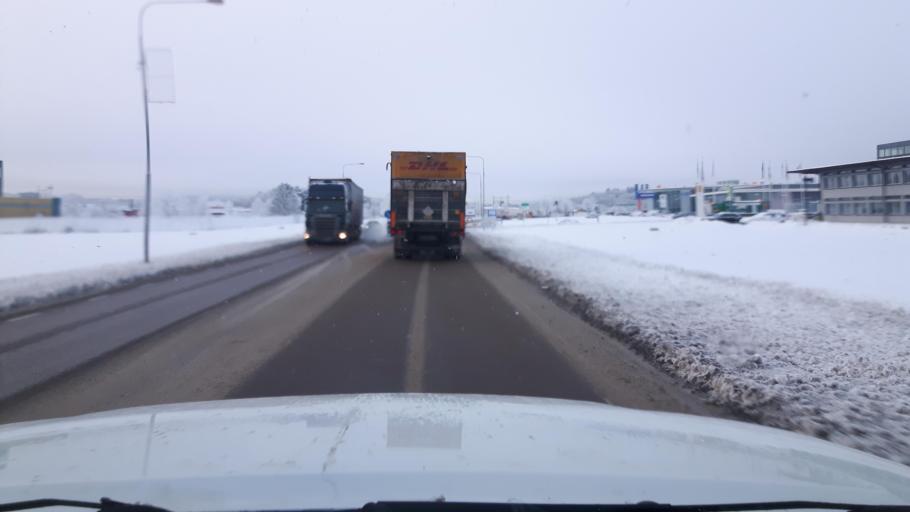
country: SE
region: Halland
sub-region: Kungsbacka Kommun
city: Kungsbacka
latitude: 57.5102
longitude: 12.0689
